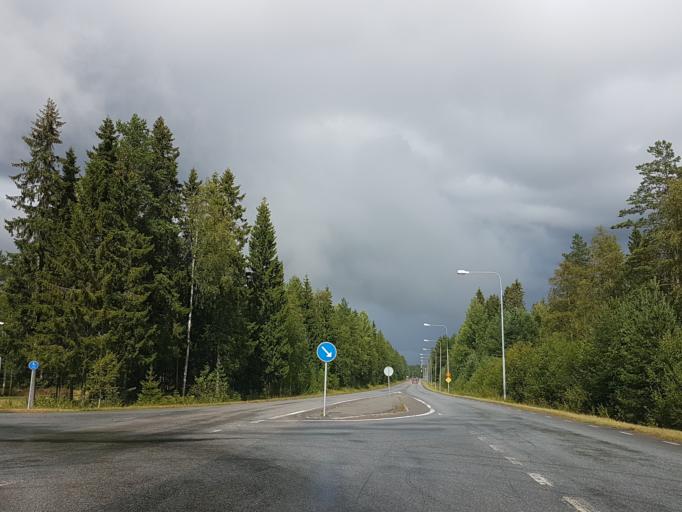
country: SE
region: Vaesterbotten
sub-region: Umea Kommun
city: Ersmark
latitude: 63.8525
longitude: 20.3439
